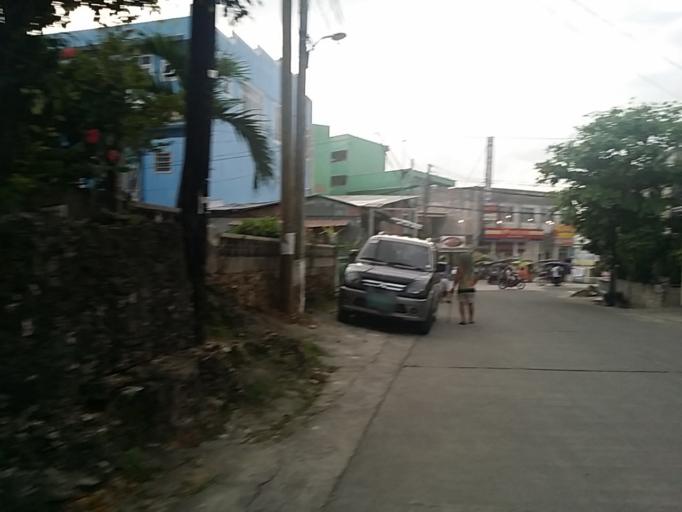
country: PH
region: Central Visayas
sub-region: Province of Cebu
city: Bogo
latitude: 11.0494
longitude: 124.0060
